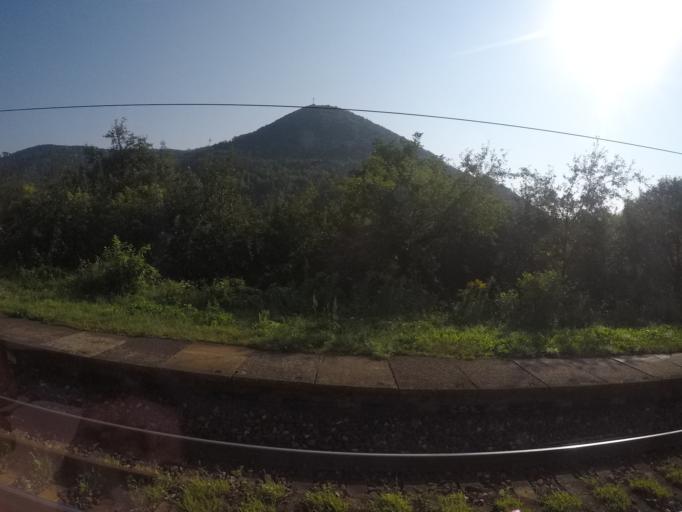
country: SK
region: Presovsky
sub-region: Okres Presov
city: Presov
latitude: 48.8561
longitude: 21.1557
